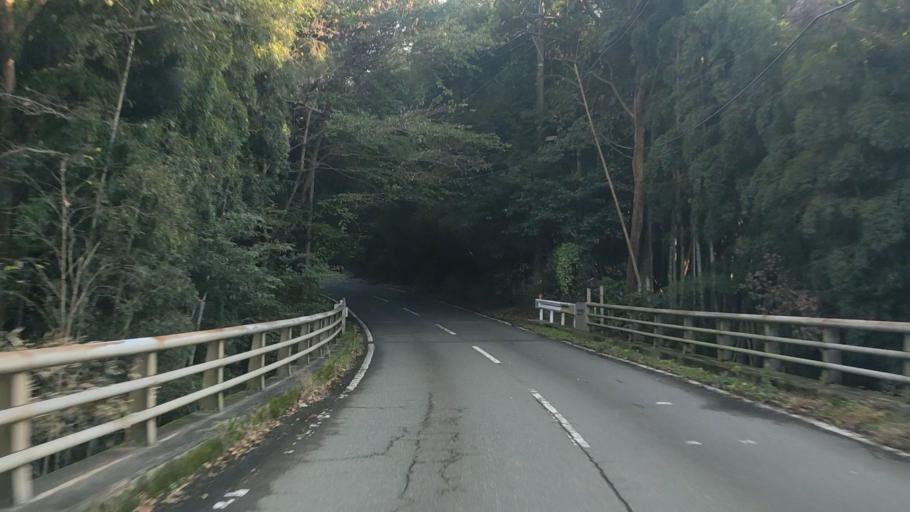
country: JP
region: Shizuoka
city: Mishima
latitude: 35.1419
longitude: 138.9449
